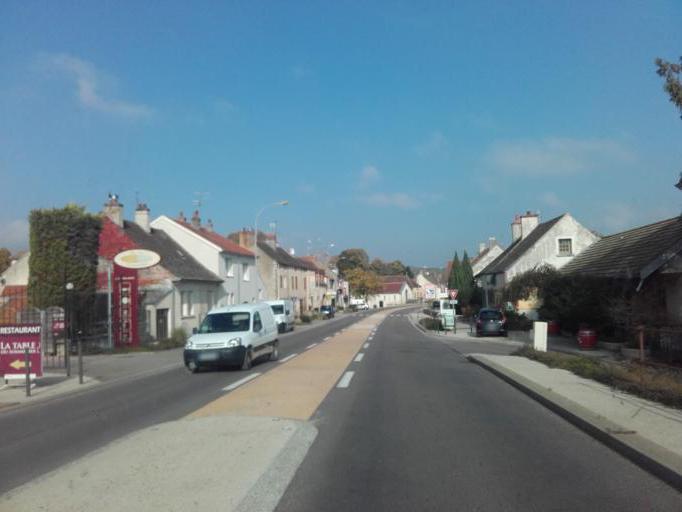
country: FR
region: Bourgogne
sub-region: Departement de la Cote-d'Or
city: Beaune
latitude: 47.0706
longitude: 4.8738
